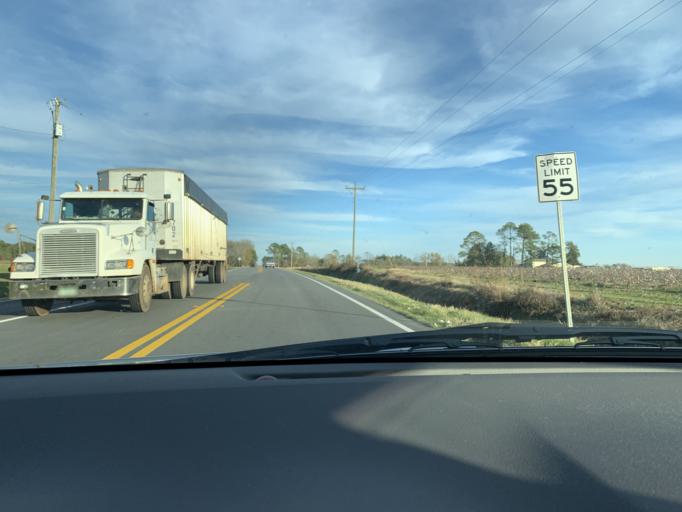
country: US
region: Georgia
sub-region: Irwin County
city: Ocilla
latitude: 31.5926
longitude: -83.2345
